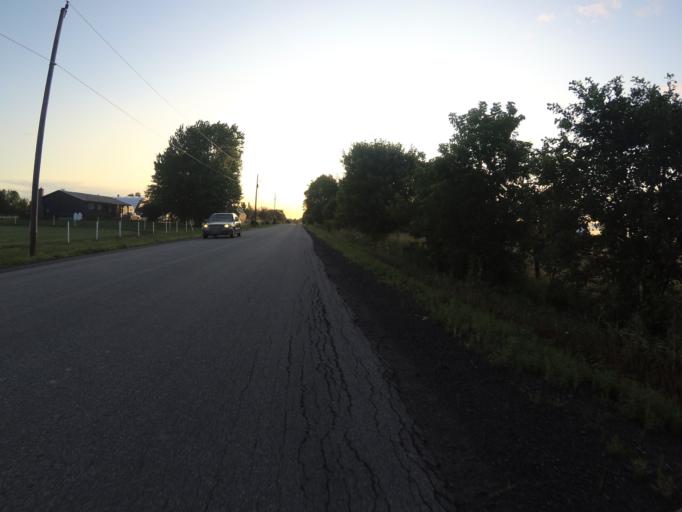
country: CA
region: Ontario
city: Ottawa
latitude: 45.1158
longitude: -75.5219
